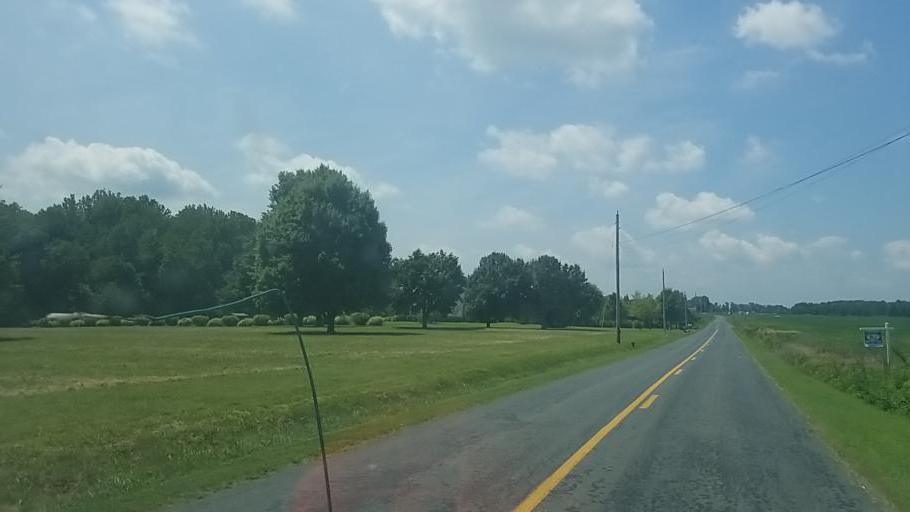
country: US
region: Maryland
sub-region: Talbot County
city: Easton
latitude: 38.7769
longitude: -76.0144
